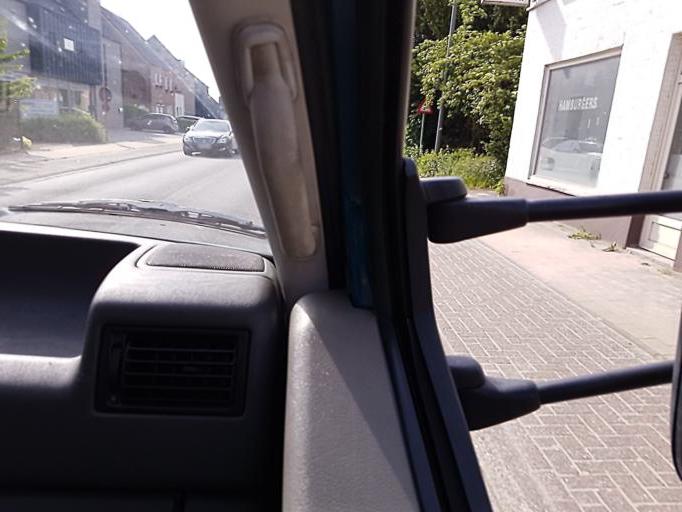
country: BE
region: Flanders
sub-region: Provincie Limburg
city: Lommel
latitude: 51.2319
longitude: 5.3354
